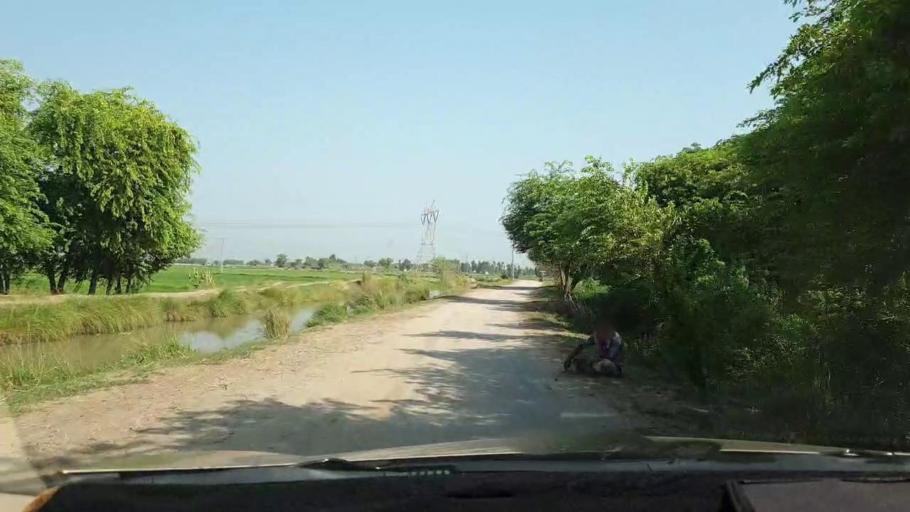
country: PK
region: Sindh
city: Larkana
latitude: 27.6364
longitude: 68.2367
